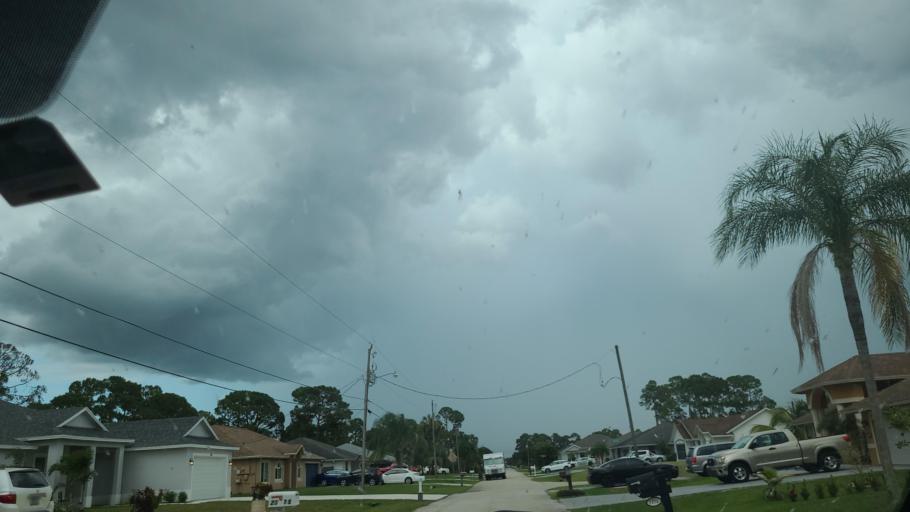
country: US
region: Florida
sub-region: Saint Lucie County
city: Port Saint Lucie
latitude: 27.2529
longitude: -80.4144
